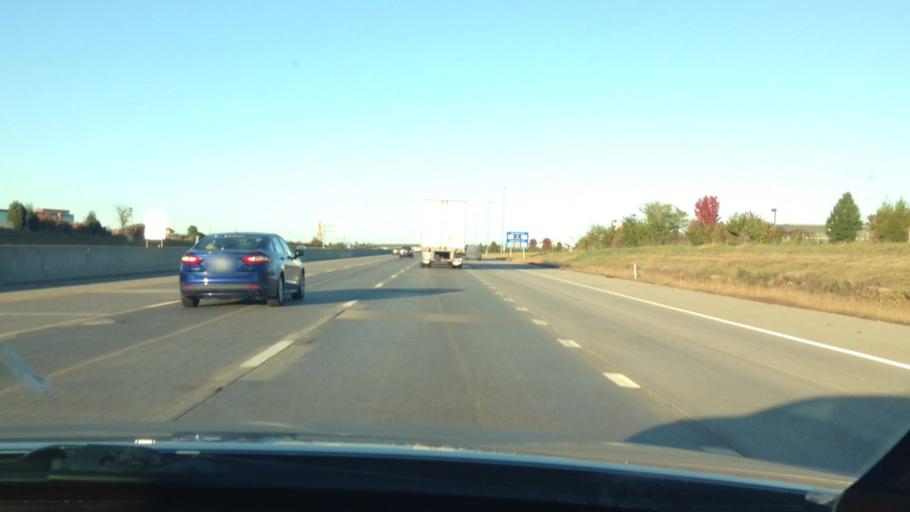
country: US
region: Kansas
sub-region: Johnson County
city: Olathe
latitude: 38.8482
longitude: -94.8243
